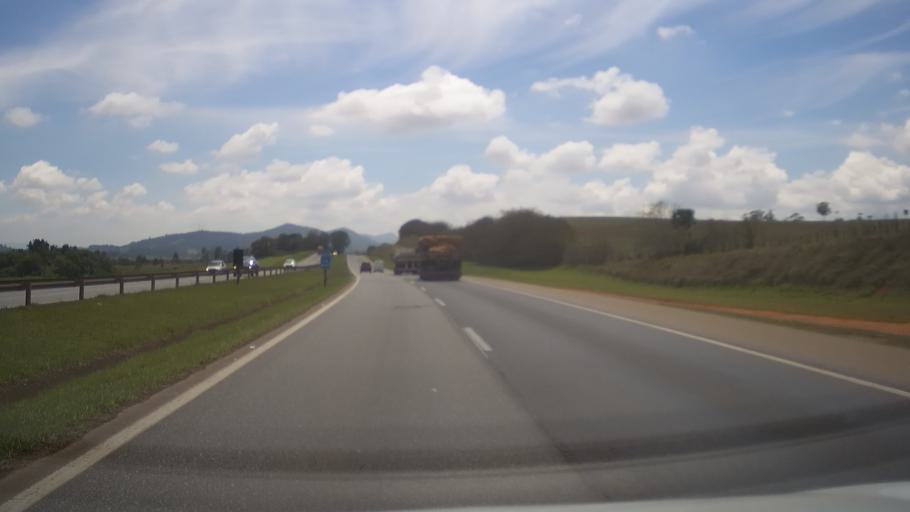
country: BR
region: Minas Gerais
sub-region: Santa Rita Do Sapucai
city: Santa Rita do Sapucai
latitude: -22.1021
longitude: -45.7234
